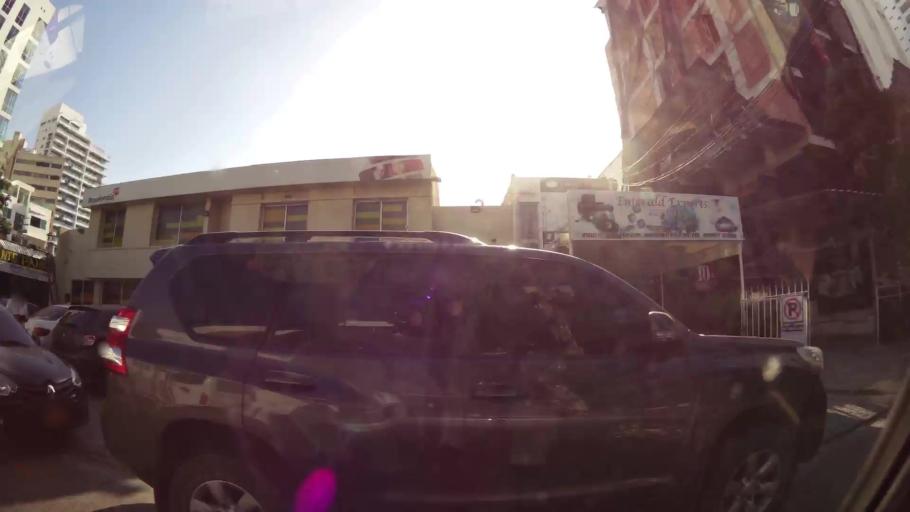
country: CO
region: Bolivar
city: Cartagena
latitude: 10.3991
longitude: -75.5588
